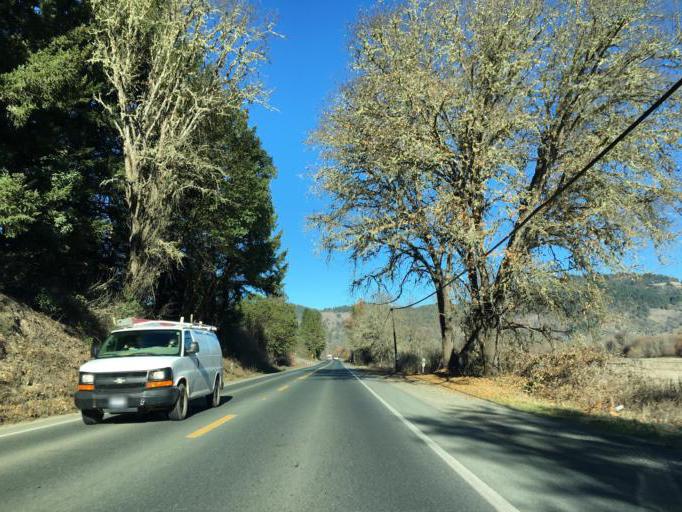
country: US
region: California
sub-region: Mendocino County
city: Brooktrails
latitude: 39.4459
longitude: -123.3512
